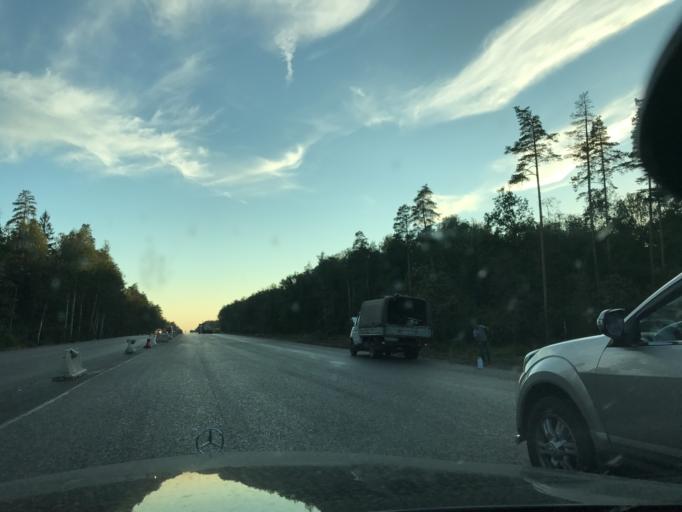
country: RU
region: Vladimir
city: Lakinsk
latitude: 55.9844
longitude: 39.8486
